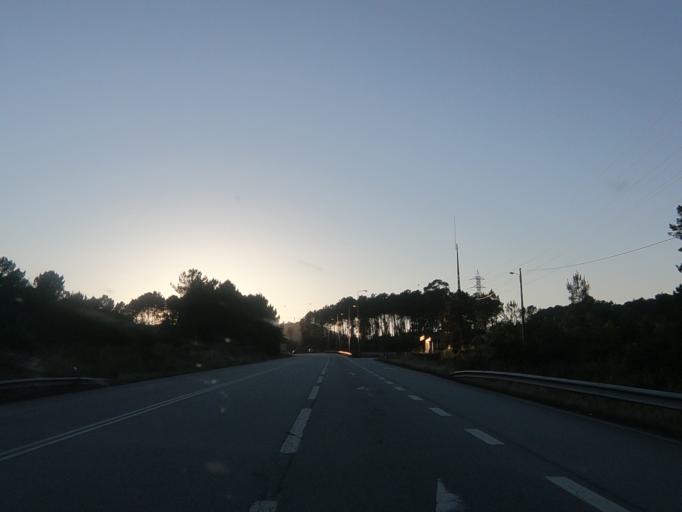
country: PT
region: Viseu
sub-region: Viseu
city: Abraveses
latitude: 40.6892
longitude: -7.9030
